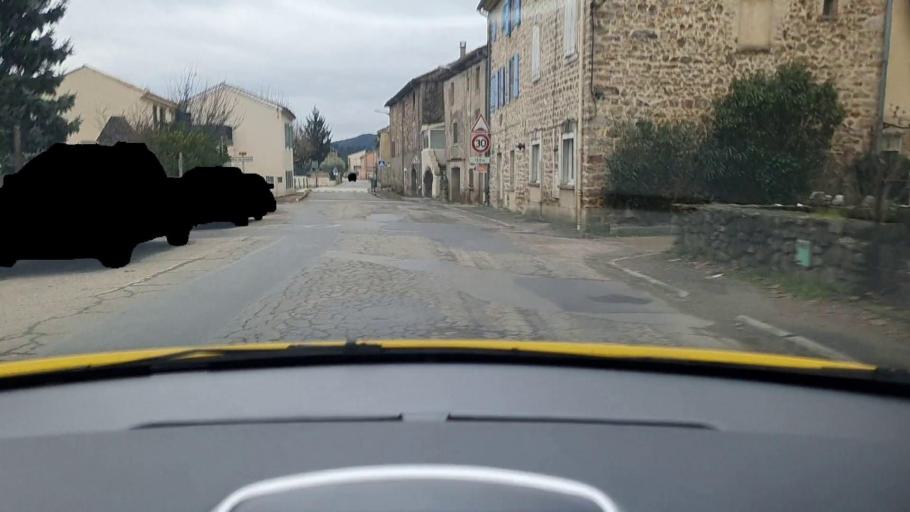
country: FR
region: Languedoc-Roussillon
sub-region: Departement du Gard
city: Laval-Pradel
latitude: 44.2318
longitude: 4.0575
